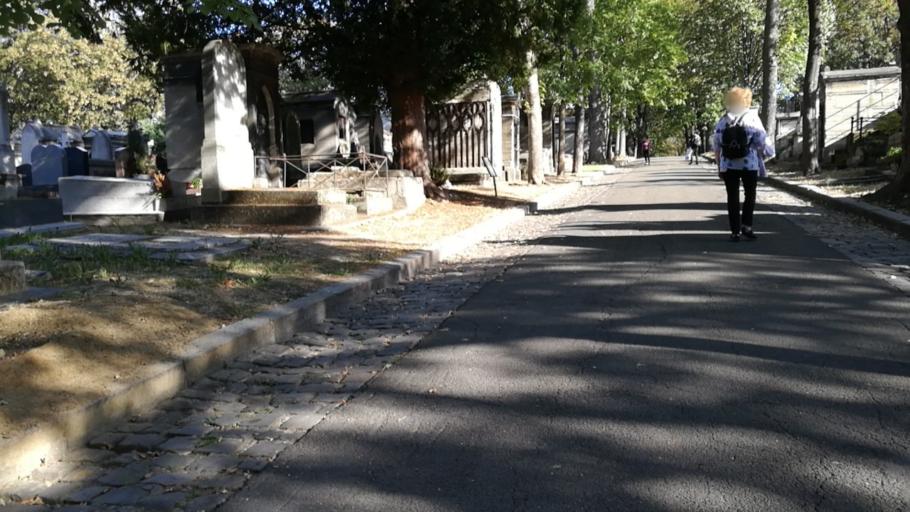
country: FR
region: Ile-de-France
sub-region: Paris
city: Saint-Ouen
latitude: 48.8879
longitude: 2.3286
